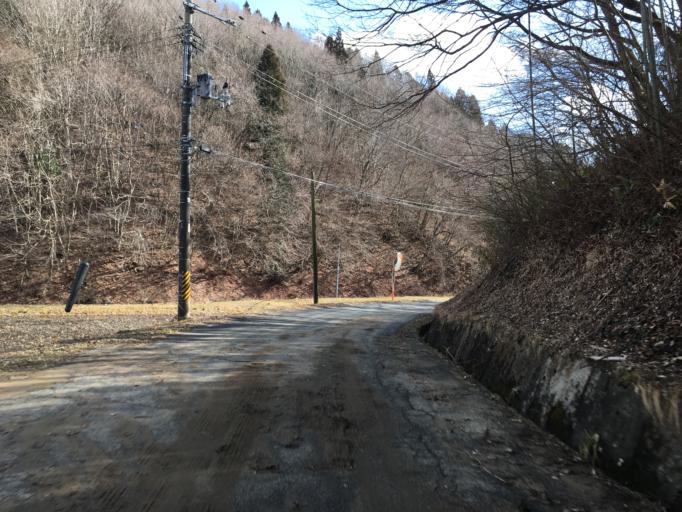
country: JP
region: Fukushima
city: Ishikawa
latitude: 37.2505
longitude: 140.5980
